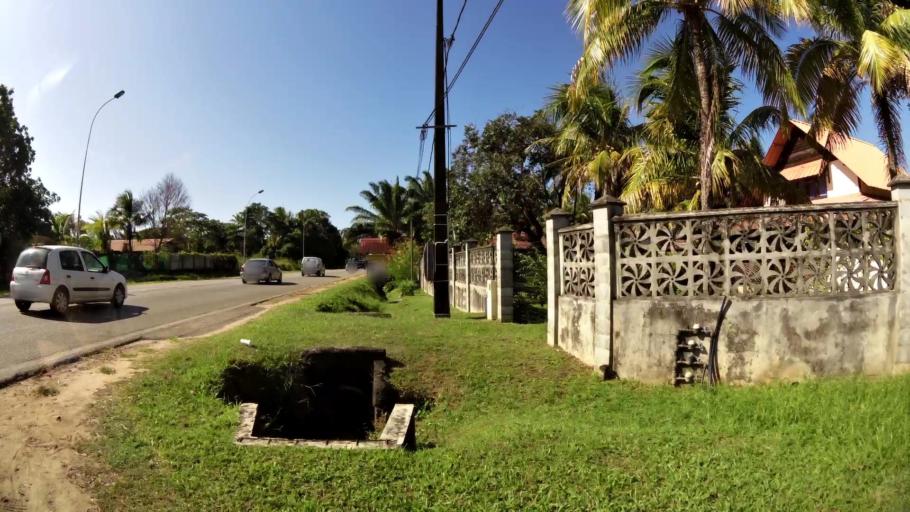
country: GF
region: Guyane
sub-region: Guyane
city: Remire-Montjoly
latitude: 4.9053
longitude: -52.2731
